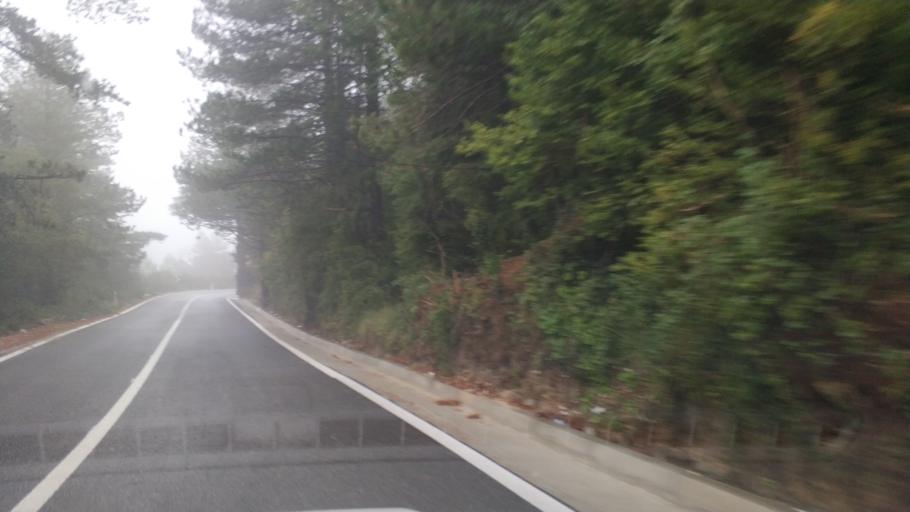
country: AL
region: Vlore
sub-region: Rrethi i Vlores
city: Vranisht
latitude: 40.2022
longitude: 19.5895
